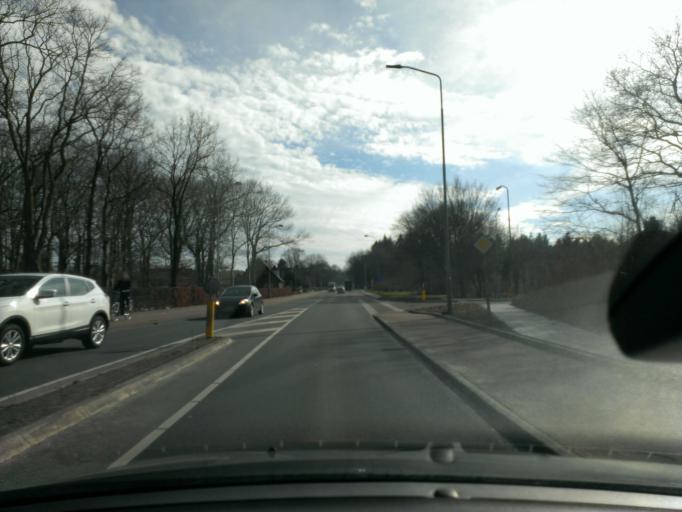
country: NL
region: Gelderland
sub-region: Gemeente Hattem
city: Hattem
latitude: 52.4576
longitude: 5.9995
